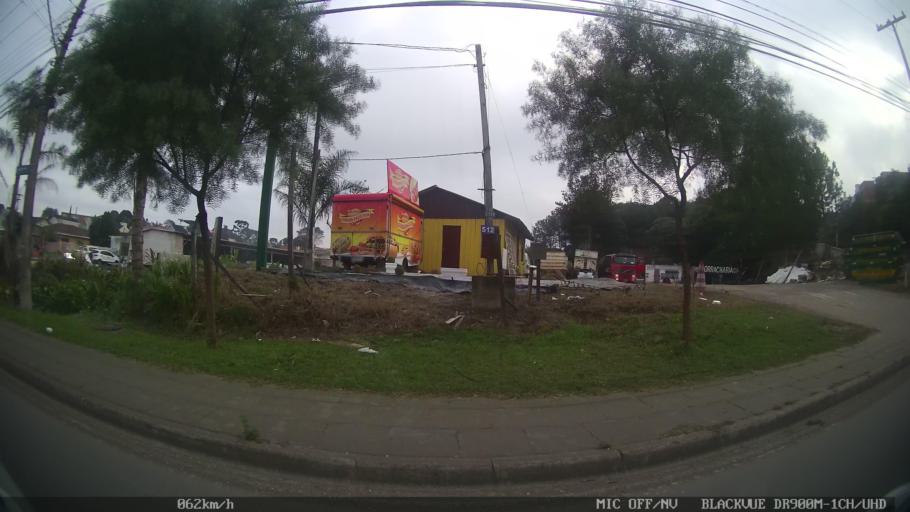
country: BR
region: Parana
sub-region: Almirante Tamandare
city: Almirante Tamandare
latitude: -25.3905
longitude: -49.3317
